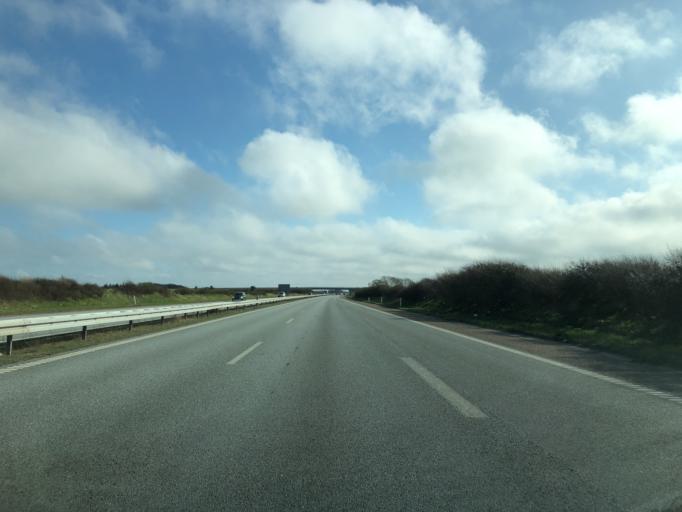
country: DK
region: North Denmark
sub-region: Hjorring Kommune
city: Hjorring
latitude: 57.4521
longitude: 10.0438
